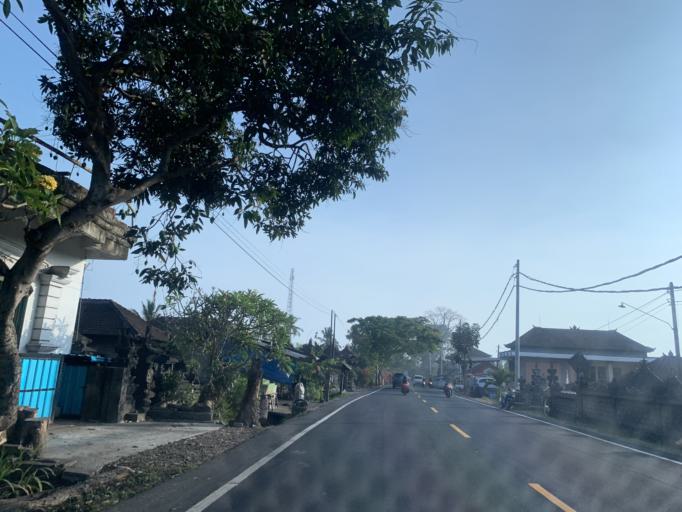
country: ID
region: Bali
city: Banjar Delodrurung
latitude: -8.4990
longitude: 115.0192
